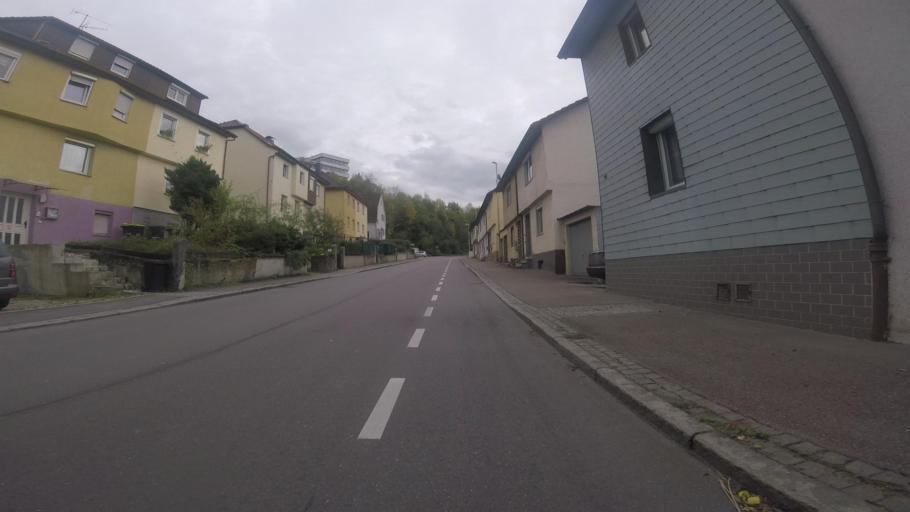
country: DE
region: Baden-Wuerttemberg
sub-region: Regierungsbezirk Stuttgart
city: Backnang
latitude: 48.9437
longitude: 9.4218
